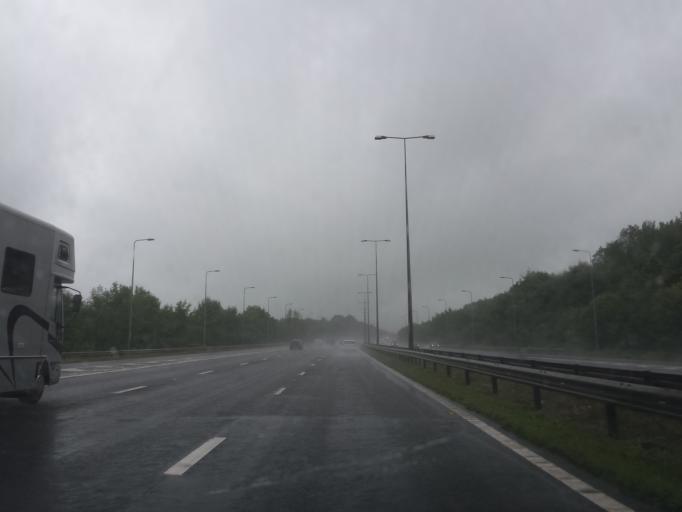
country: GB
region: England
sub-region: Leicestershire
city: Shepshed
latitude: 52.7572
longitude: -1.2740
